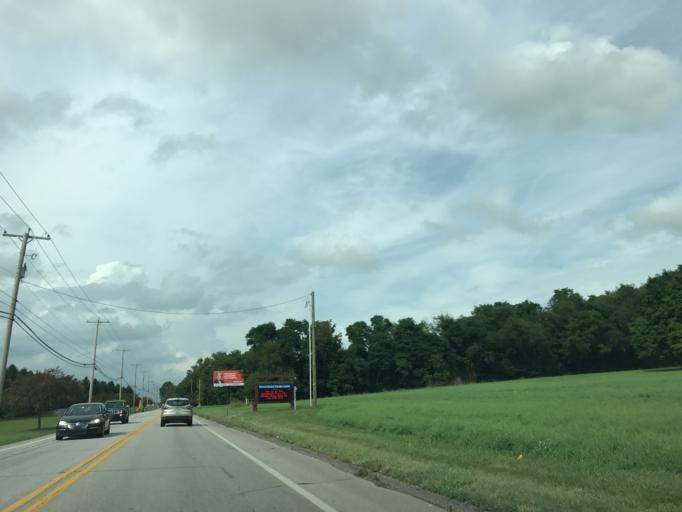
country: US
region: Pennsylvania
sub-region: York County
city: Spring Grove
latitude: 39.8873
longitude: -76.8603
